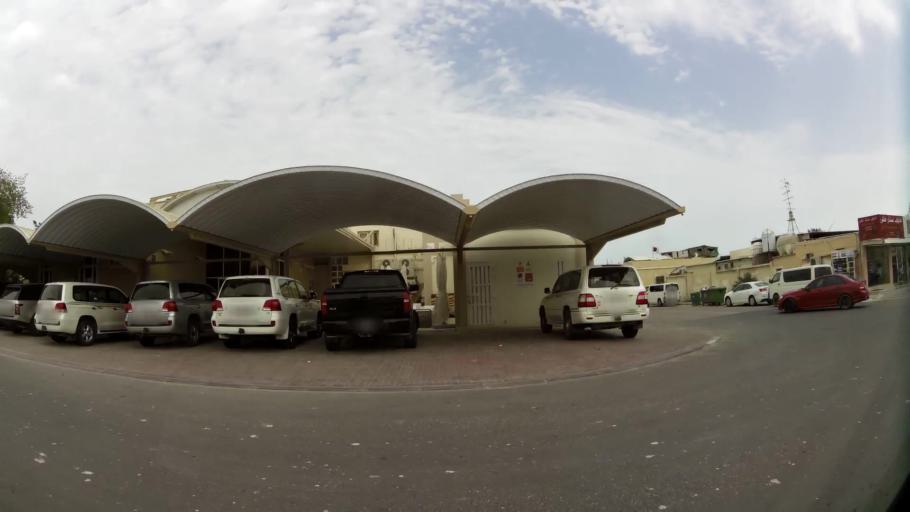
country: QA
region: Baladiyat ar Rayyan
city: Ar Rayyan
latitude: 25.3257
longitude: 51.4698
